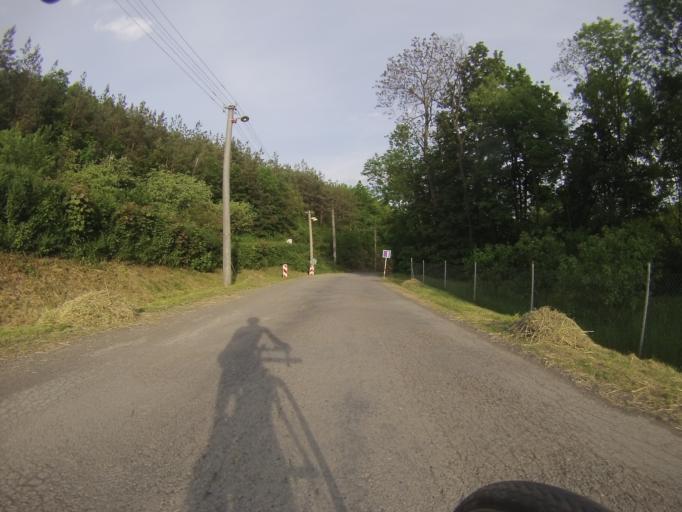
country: CZ
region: Olomoucky
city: Pteni
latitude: 49.4736
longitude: 16.9653
